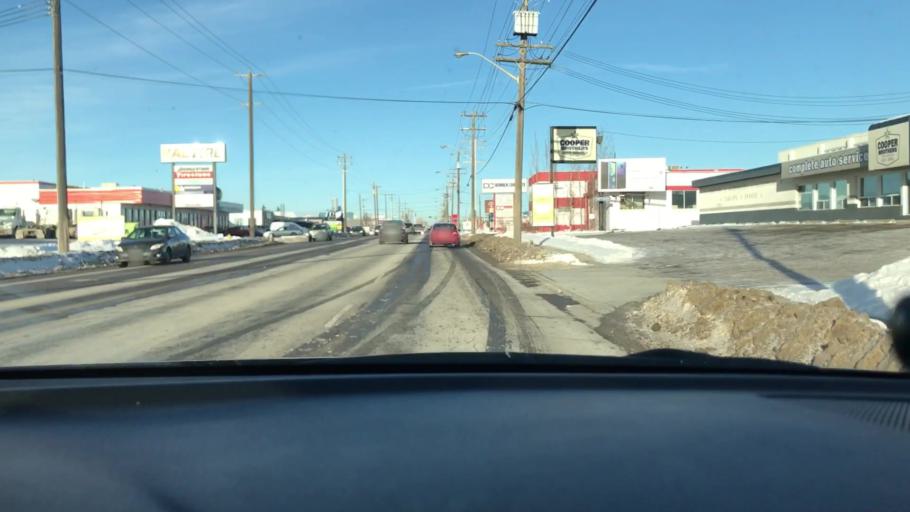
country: CA
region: Alberta
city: Edmonton
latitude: 53.4934
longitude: -113.4861
